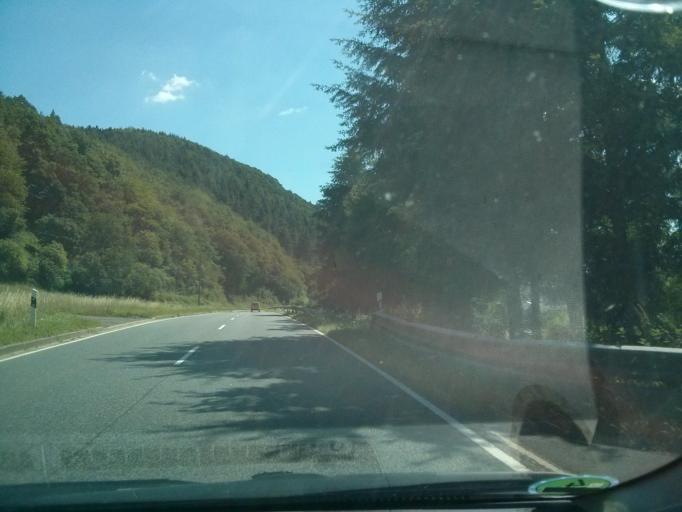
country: DE
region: Rheinland-Pfalz
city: Insul
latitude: 50.4347
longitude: 6.9333
